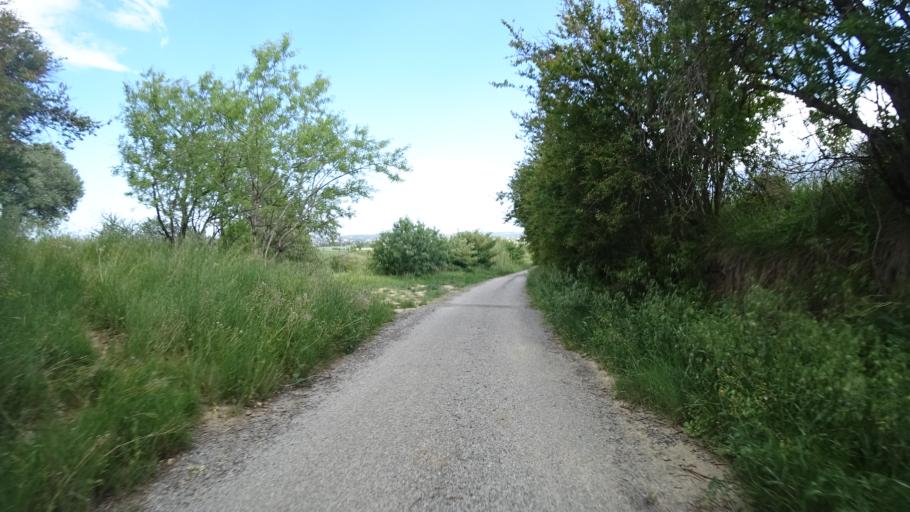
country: FR
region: Languedoc-Roussillon
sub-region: Departement de l'Aude
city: Ginestas
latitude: 43.2628
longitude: 2.8755
